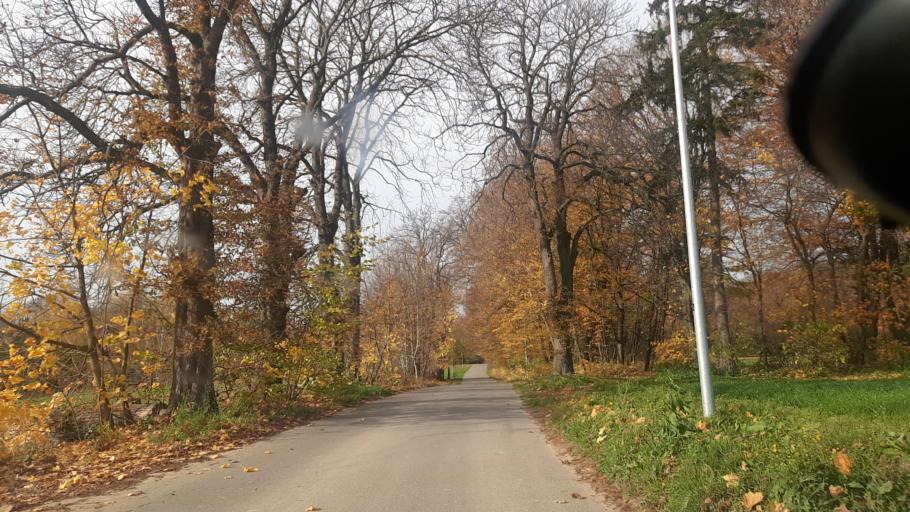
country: PL
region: Lublin Voivodeship
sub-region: Powiat lubelski
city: Jastkow
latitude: 51.3397
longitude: 22.4179
